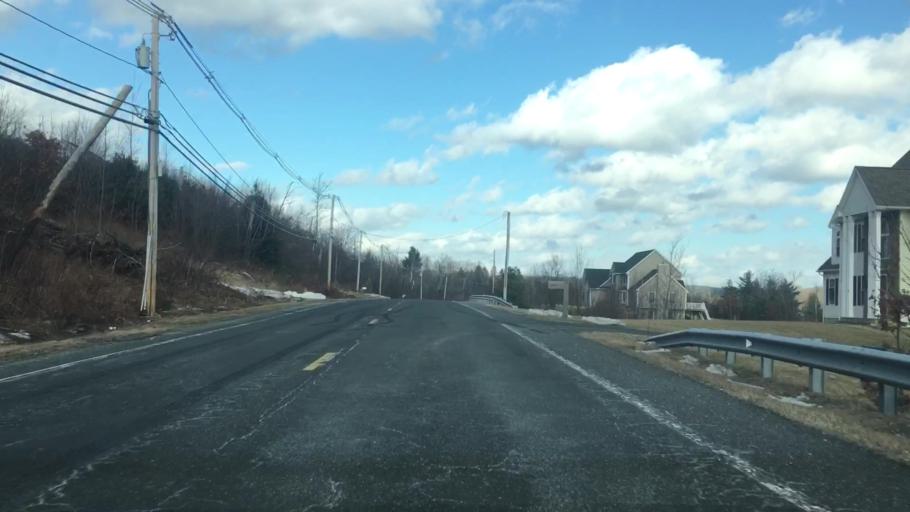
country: US
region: Massachusetts
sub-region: Hampden County
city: Brimfield
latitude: 42.1088
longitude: -72.2021
